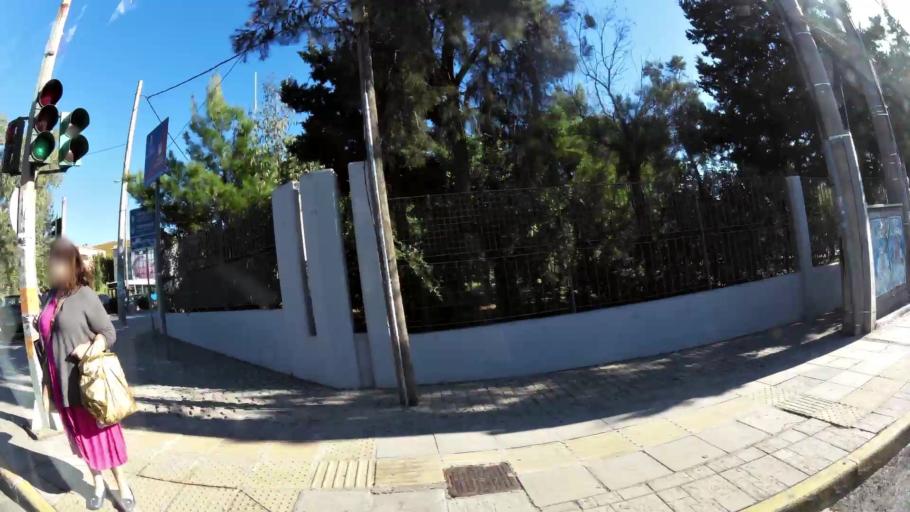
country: GR
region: Attica
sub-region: Nomarchia Athinas
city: Melissia
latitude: 38.0465
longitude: 23.8394
